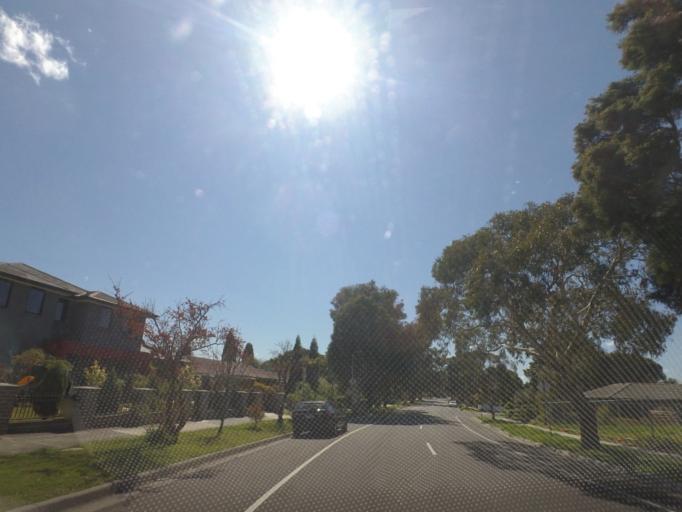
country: AU
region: Victoria
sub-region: Knox
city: Wantirna South
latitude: -37.8818
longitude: 145.2231
